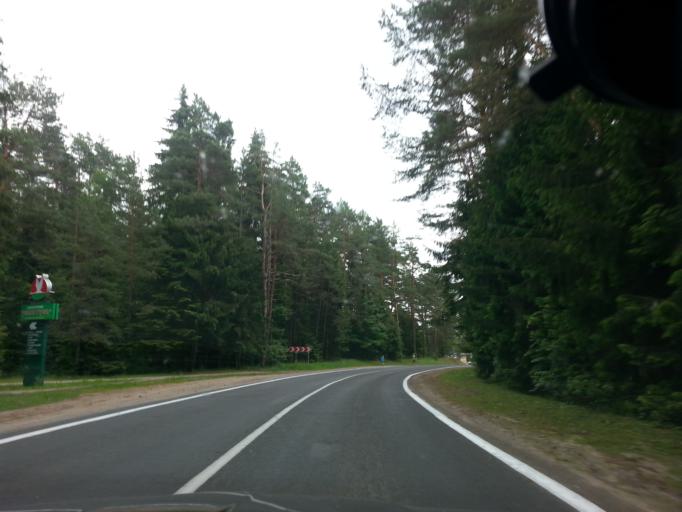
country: BY
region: Minsk
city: Narach
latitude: 54.9090
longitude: 26.7292
